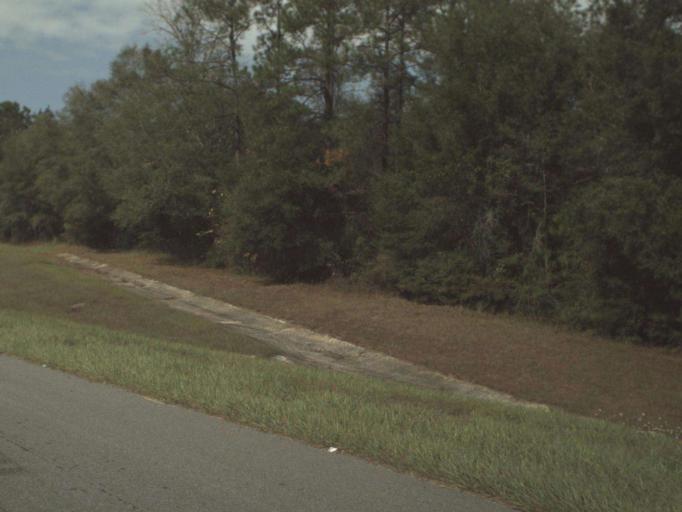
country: US
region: Florida
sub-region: Gadsden County
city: Gretna
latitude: 30.6108
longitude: -84.7488
